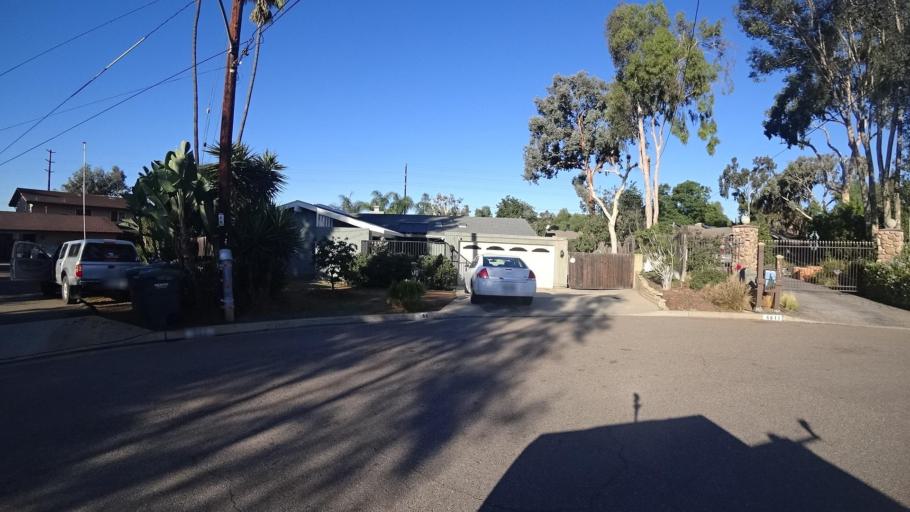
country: US
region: California
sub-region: San Diego County
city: Bonita
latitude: 32.6720
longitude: -117.0281
